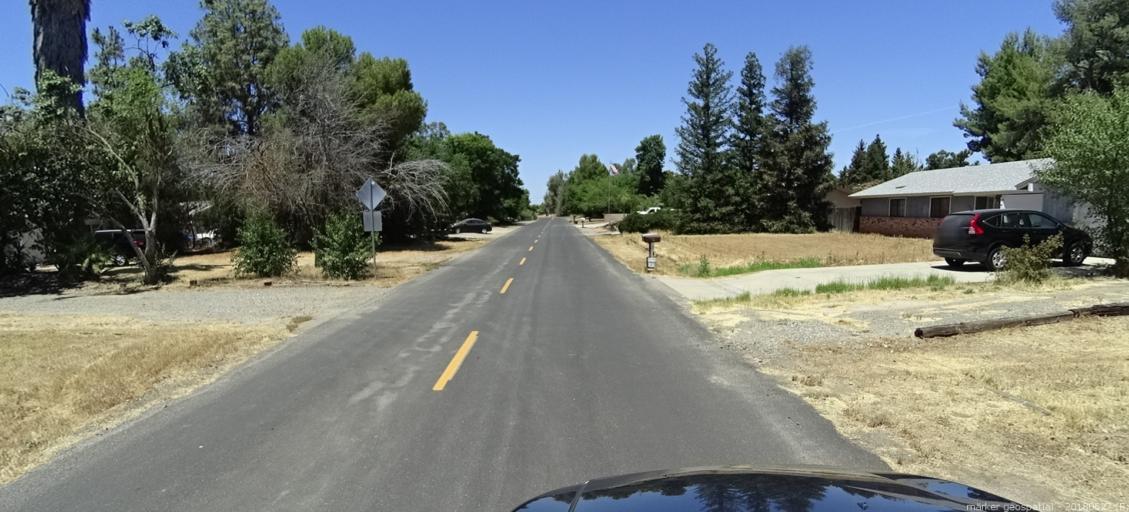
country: US
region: California
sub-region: Madera County
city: Bonadelle Ranchos-Madera Ranchos
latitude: 36.9270
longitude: -119.8809
